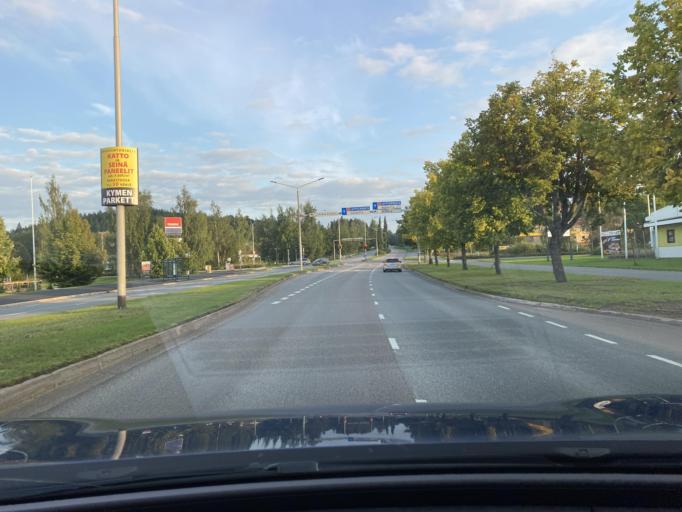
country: FI
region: Kymenlaakso
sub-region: Kouvola
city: Kouvola
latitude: 60.9025
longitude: 26.6297
